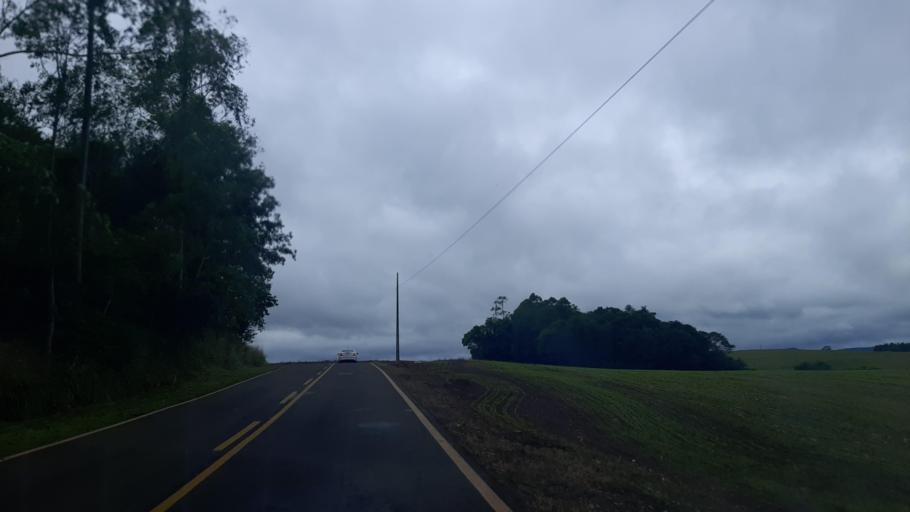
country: BR
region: Parana
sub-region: Ampere
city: Ampere
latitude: -25.9545
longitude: -53.4536
